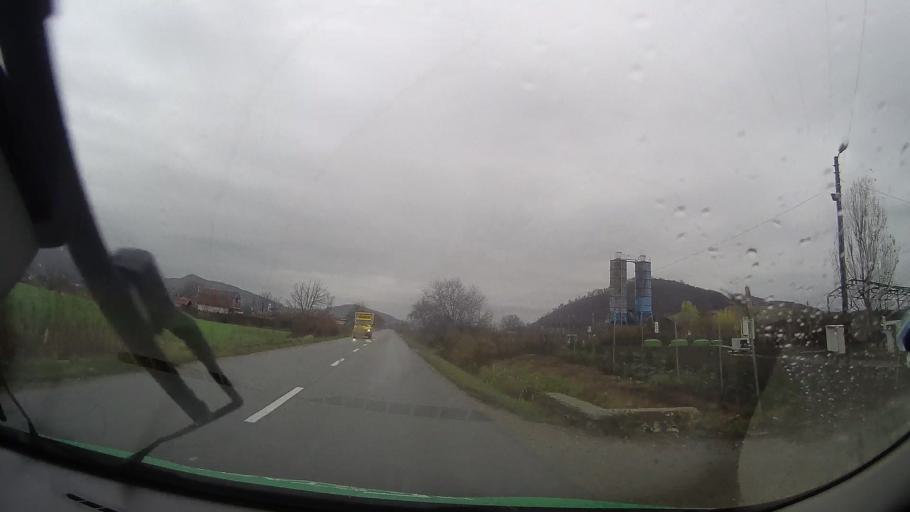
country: RO
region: Bistrita-Nasaud
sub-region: Municipiul Bistrita
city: Viisoara
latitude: 47.0623
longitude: 24.4365
